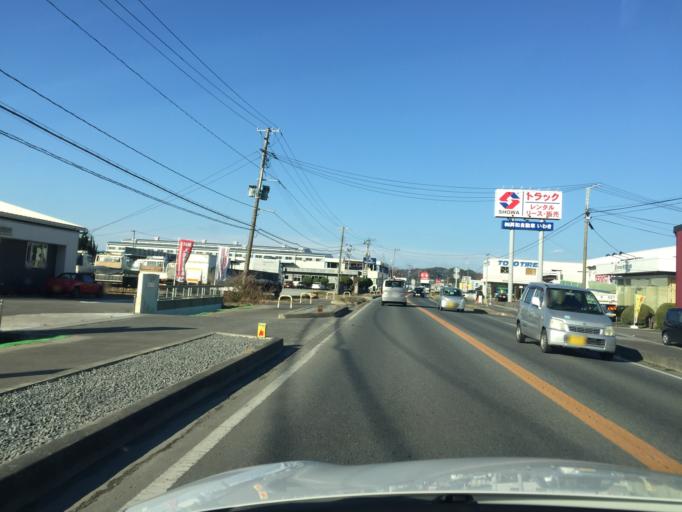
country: JP
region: Fukushima
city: Iwaki
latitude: 36.9733
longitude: 140.8702
